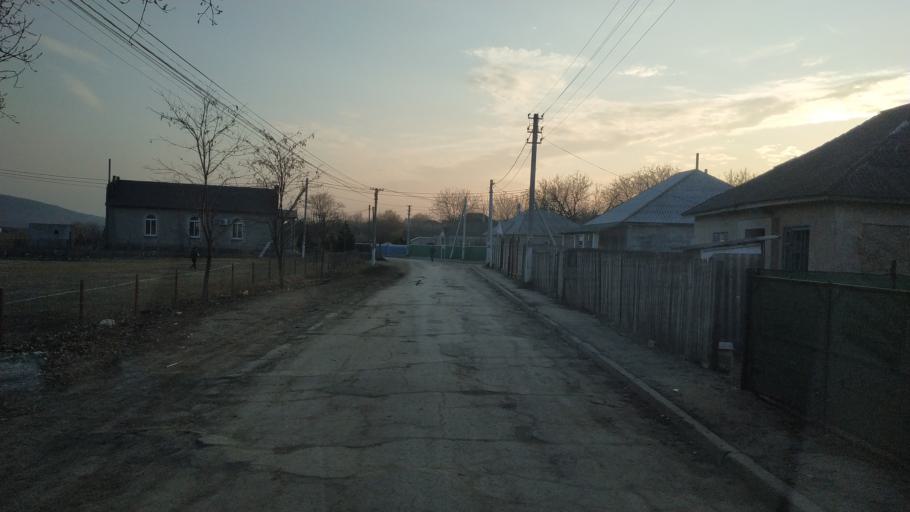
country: MD
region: Hincesti
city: Dancu
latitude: 46.7116
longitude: 28.3462
